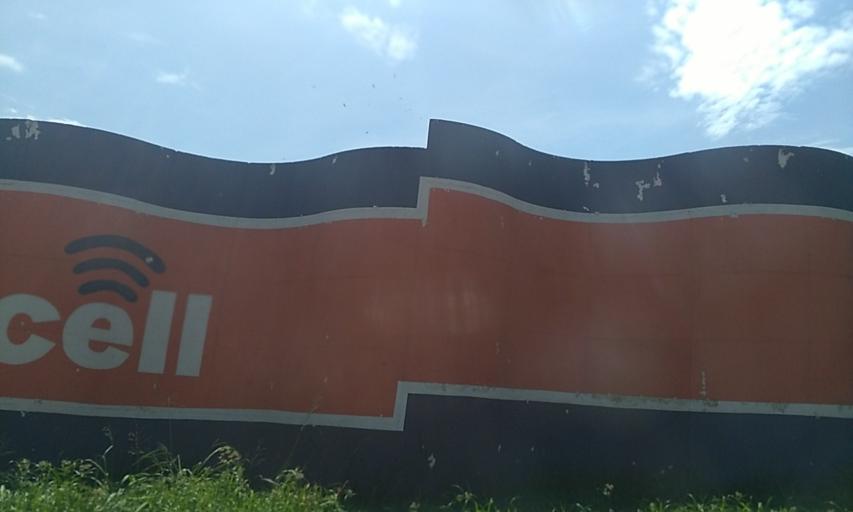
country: UG
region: Central Region
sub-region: Kampala District
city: Kampala
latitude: 0.3266
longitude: 32.6044
